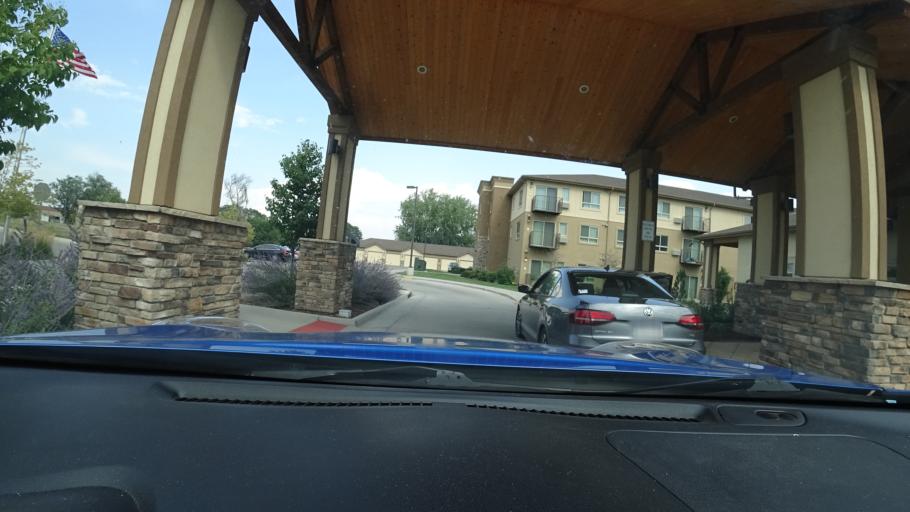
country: US
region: Colorado
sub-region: Boulder County
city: Lafayette
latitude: 39.9992
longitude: -105.1006
